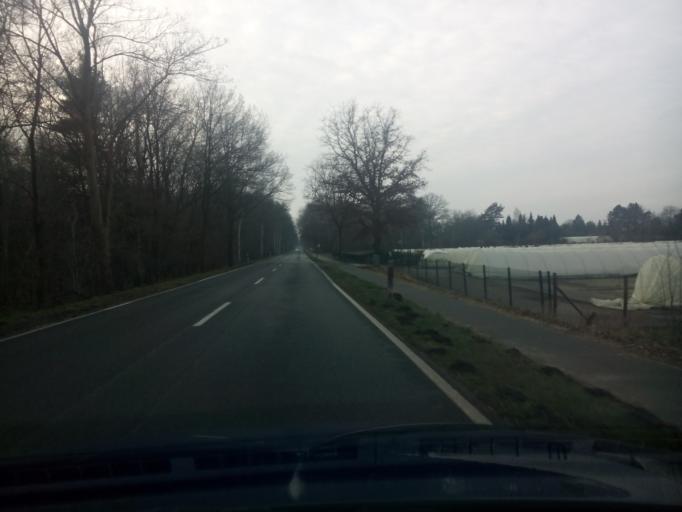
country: DE
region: Lower Saxony
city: Grasberg
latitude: 53.1284
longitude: 9.0205
